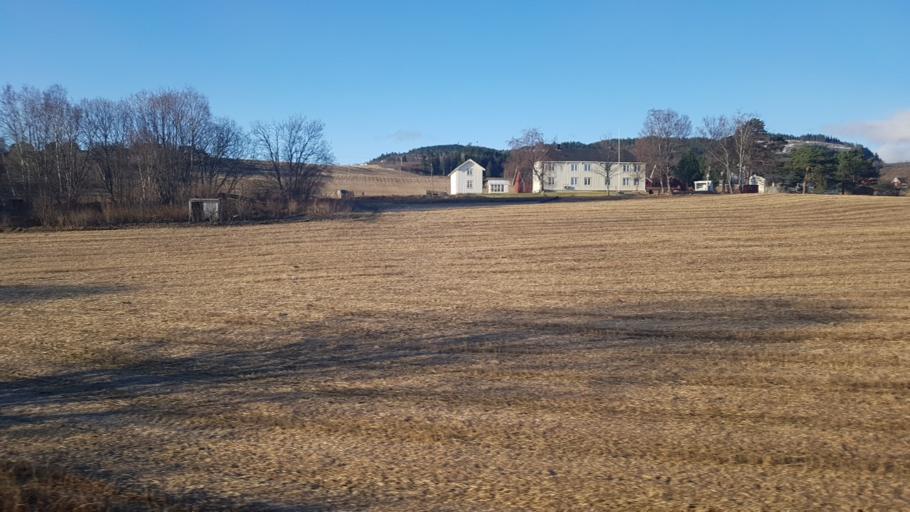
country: NO
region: Sor-Trondelag
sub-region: Malvik
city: Malvik
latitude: 63.4312
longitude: 10.6929
